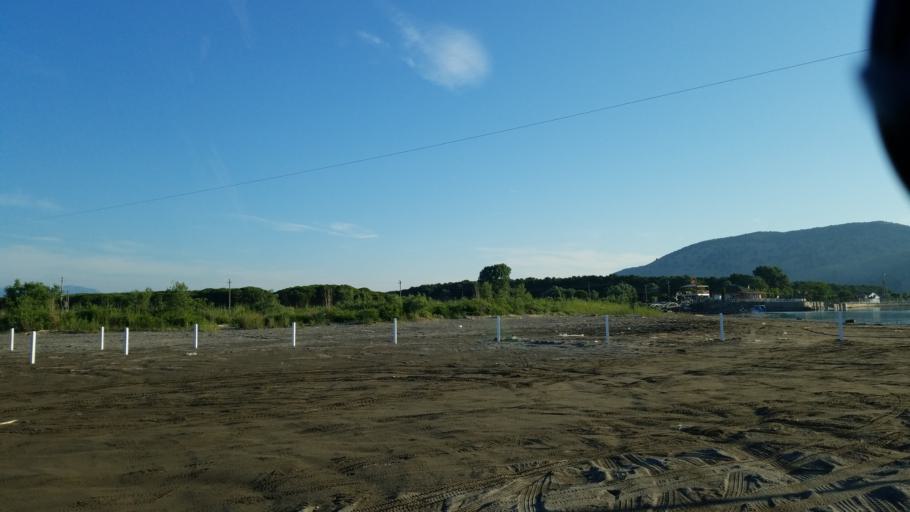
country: AL
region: Shkoder
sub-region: Rrethi i Shkodres
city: Velipoje
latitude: 41.8592
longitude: 19.4458
